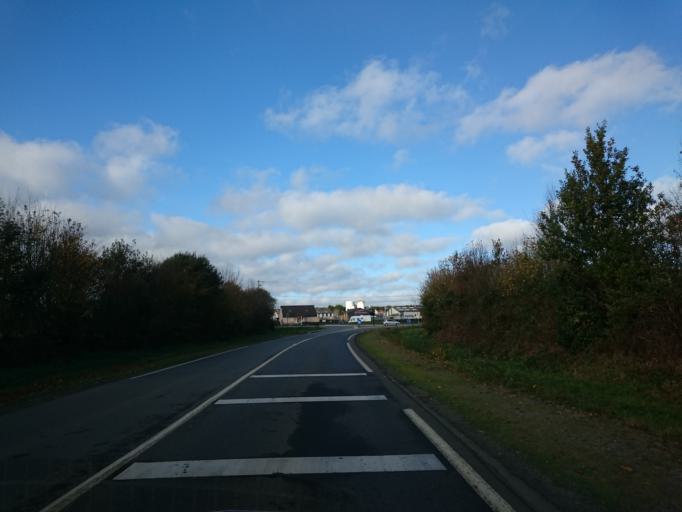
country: FR
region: Brittany
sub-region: Departement d'Ille-et-Vilaine
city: Bain-de-Bretagne
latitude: 47.8530
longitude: -1.6780
